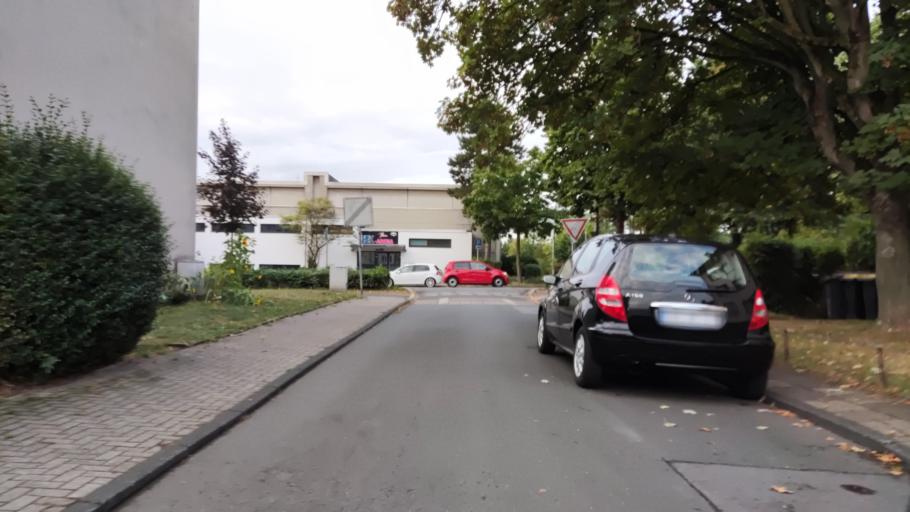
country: DE
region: North Rhine-Westphalia
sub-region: Regierungsbezirk Arnsberg
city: Herne
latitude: 51.5393
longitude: 7.2466
